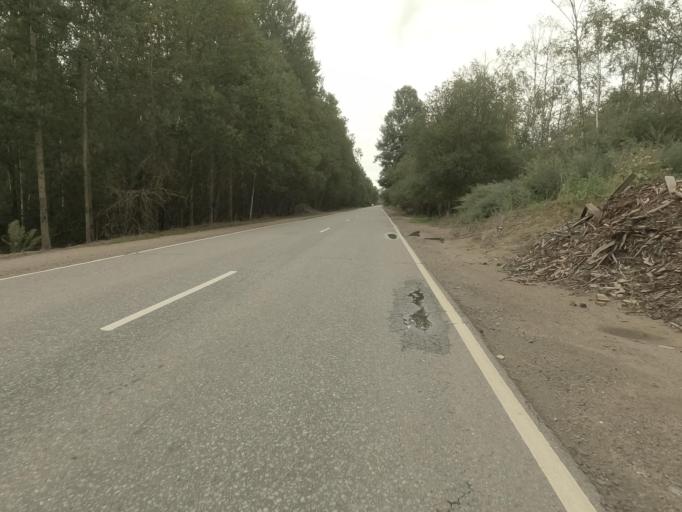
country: RU
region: Leningrad
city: Koltushi
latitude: 59.9009
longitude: 30.7685
